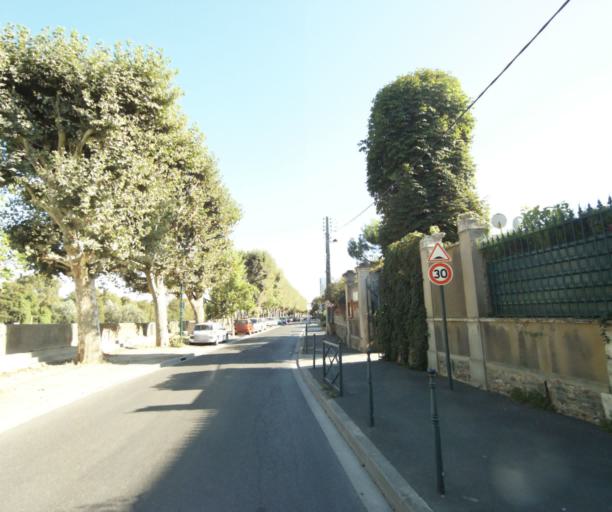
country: FR
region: Ile-de-France
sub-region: Departement de Seine-Saint-Denis
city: Villetaneuse
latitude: 48.9393
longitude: 2.3353
